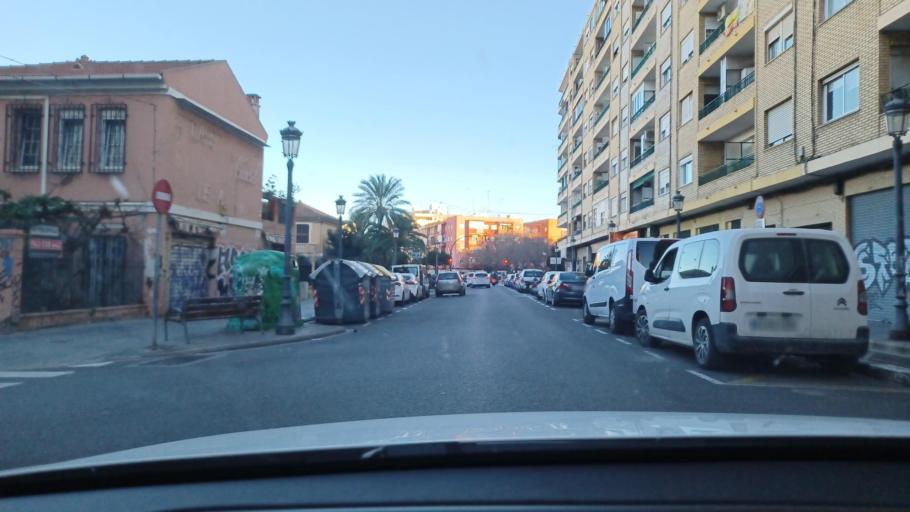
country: ES
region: Valencia
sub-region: Provincia de Valencia
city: Valencia
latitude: 39.4536
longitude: -0.3896
